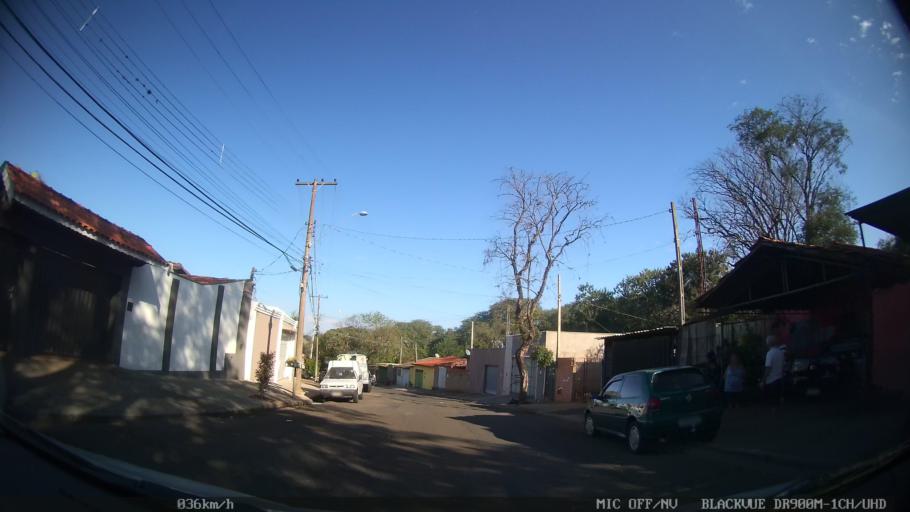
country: BR
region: Sao Paulo
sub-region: Piracicaba
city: Piracicaba
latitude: -22.6864
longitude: -47.6353
